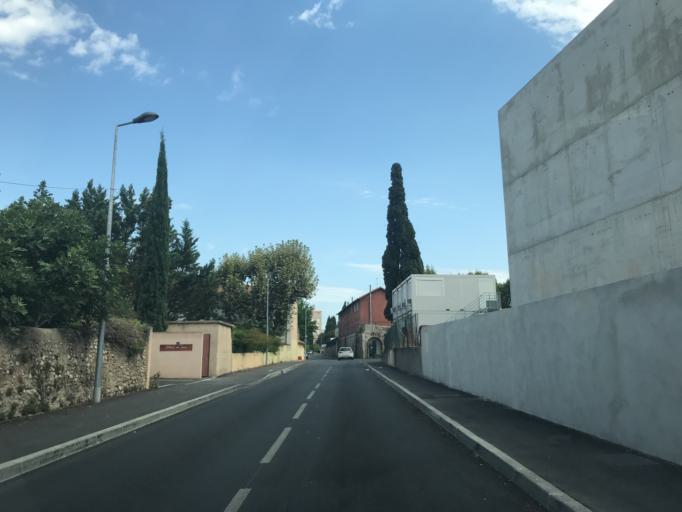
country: FR
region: Provence-Alpes-Cote d'Azur
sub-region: Departement des Bouches-du-Rhone
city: Aix-en-Provence
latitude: 43.5208
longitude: 5.4375
